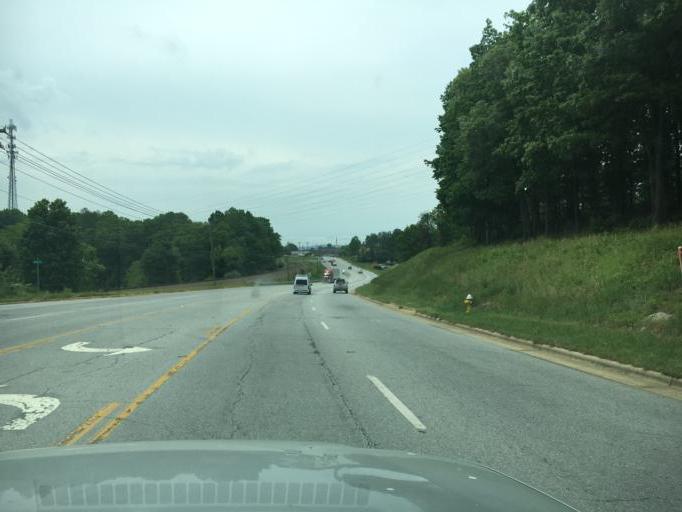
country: US
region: North Carolina
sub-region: Henderson County
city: Balfour
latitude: 35.3573
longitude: -82.4767
